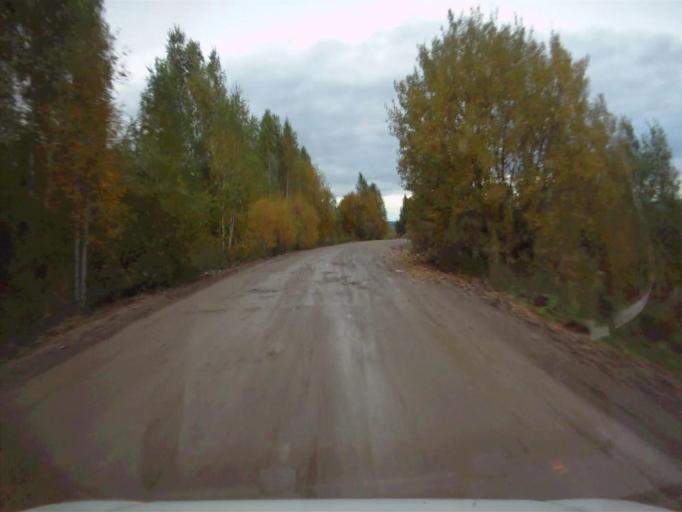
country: RU
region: Sverdlovsk
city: Mikhaylovsk
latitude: 56.2010
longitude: 59.2004
